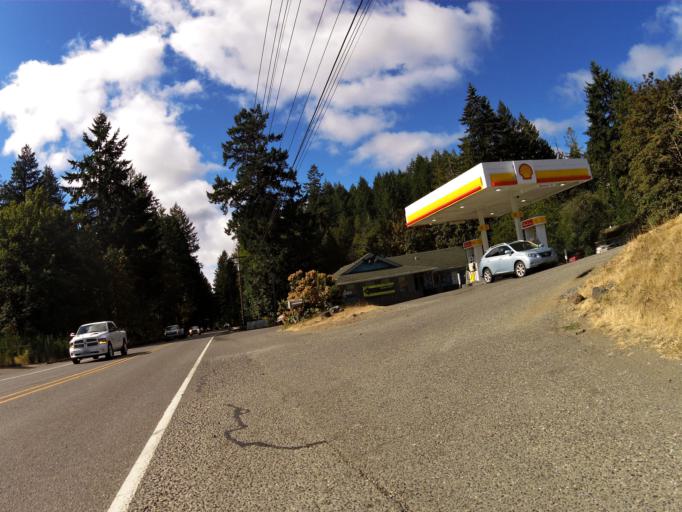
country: US
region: Washington
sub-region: Mason County
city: Shelton
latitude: 47.2488
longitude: -123.0445
